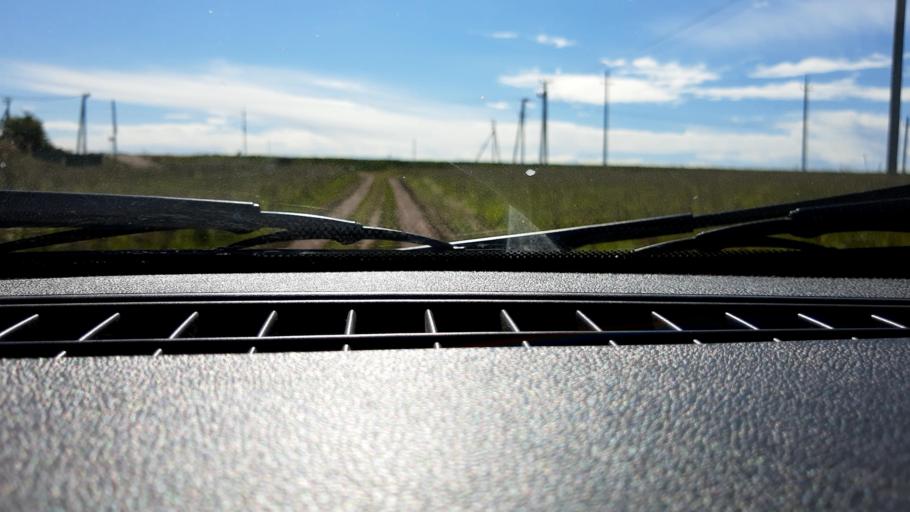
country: RU
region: Bashkortostan
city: Mikhaylovka
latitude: 54.8189
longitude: 55.7881
